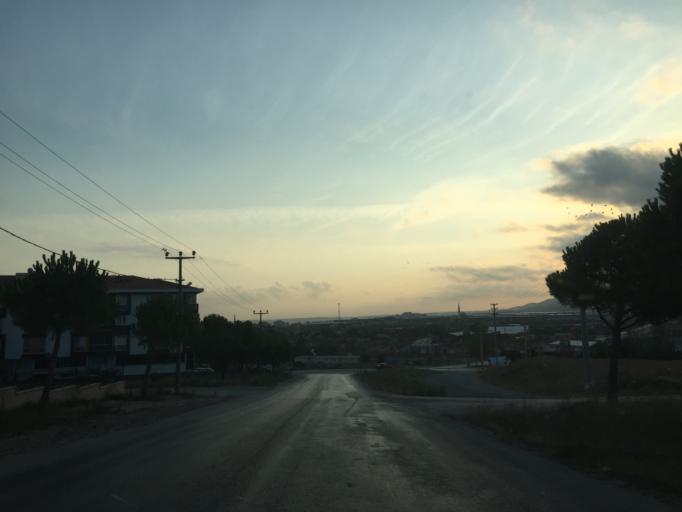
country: TR
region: Balikesir
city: Gonen
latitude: 40.0966
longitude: 27.6627
